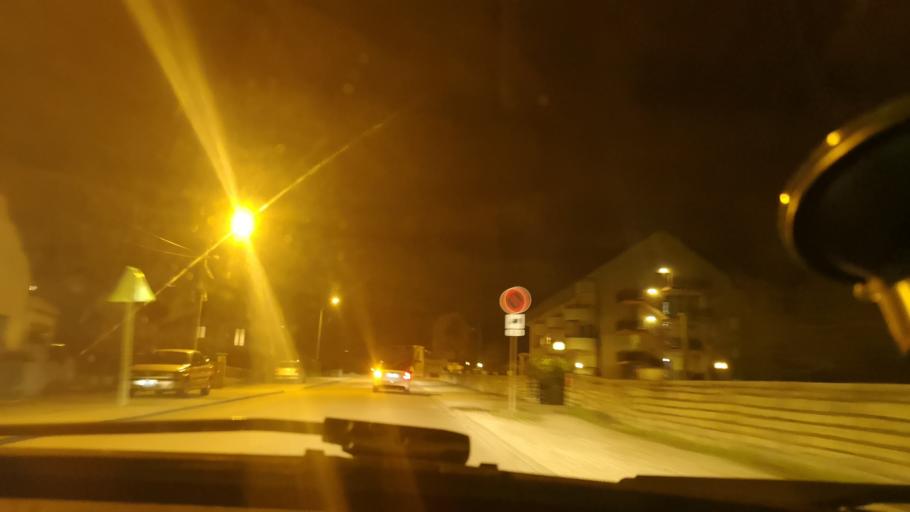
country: FR
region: Bourgogne
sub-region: Departement de Saone-et-Loire
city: Saint-Remy
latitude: 46.7604
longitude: 4.8416
